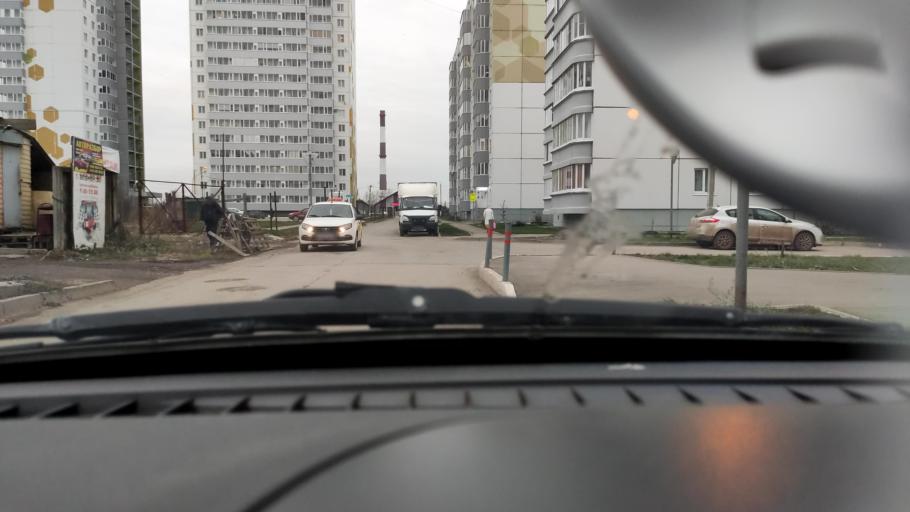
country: RU
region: Perm
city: Kondratovo
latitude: 57.9876
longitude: 56.1178
